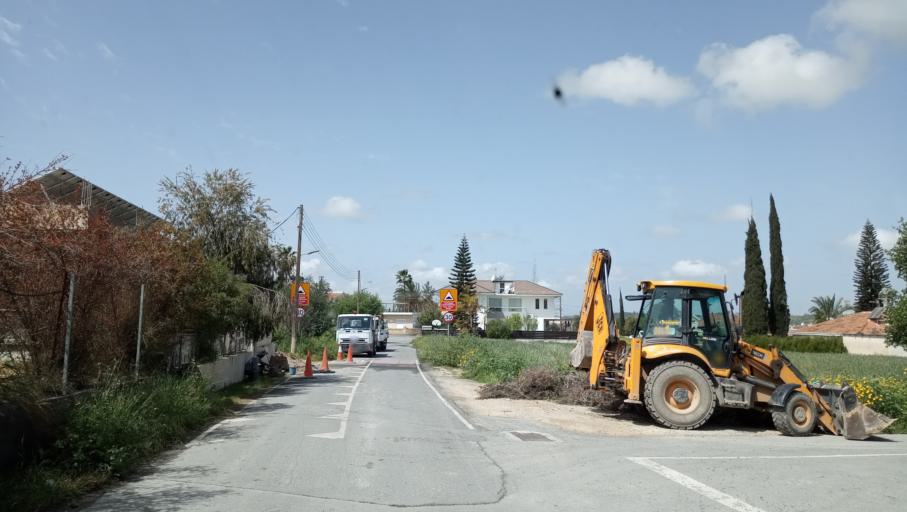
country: CY
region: Lefkosia
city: Dali
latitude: 35.0150
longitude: 33.4144
